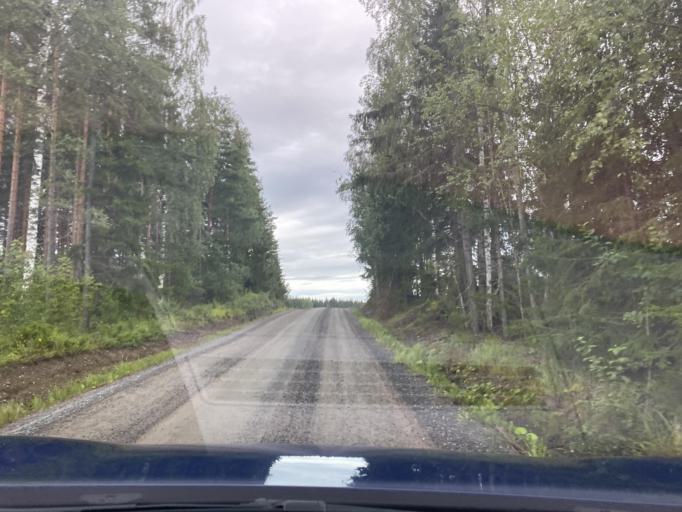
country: FI
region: Pirkanmaa
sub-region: Lounais-Pirkanmaa
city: Punkalaidun
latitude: 61.2470
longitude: 23.0442
